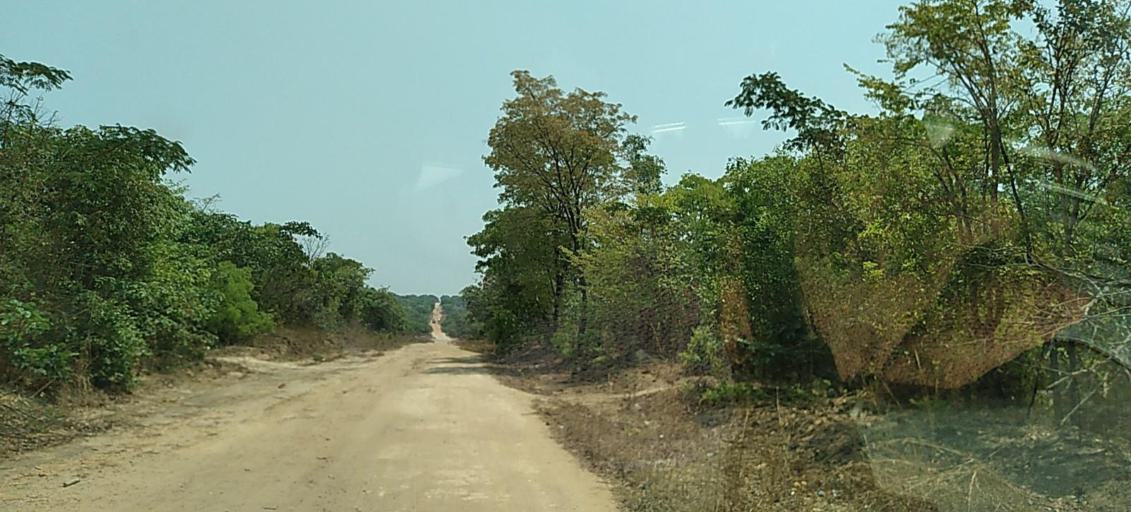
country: ZM
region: Copperbelt
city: Kalulushi
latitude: -12.9361
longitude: 28.1621
